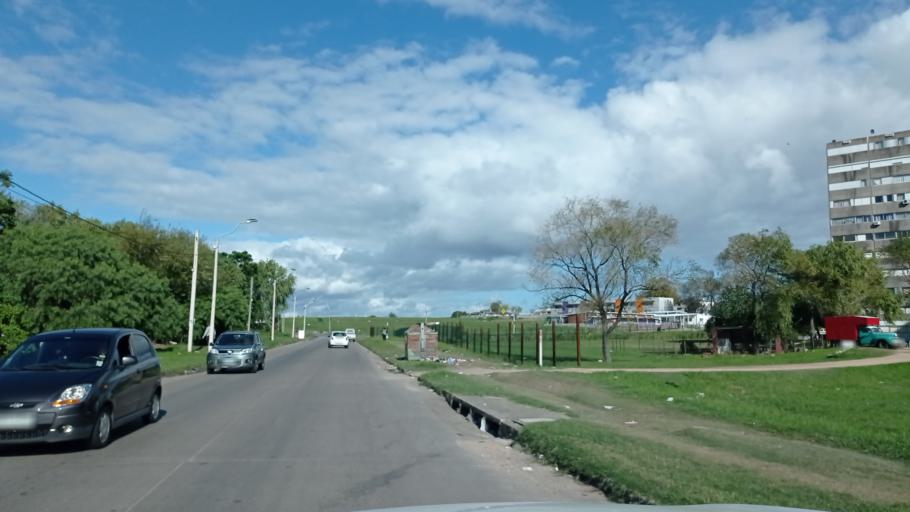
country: UY
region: Canelones
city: Paso de Carrasco
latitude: -34.8766
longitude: -56.1171
